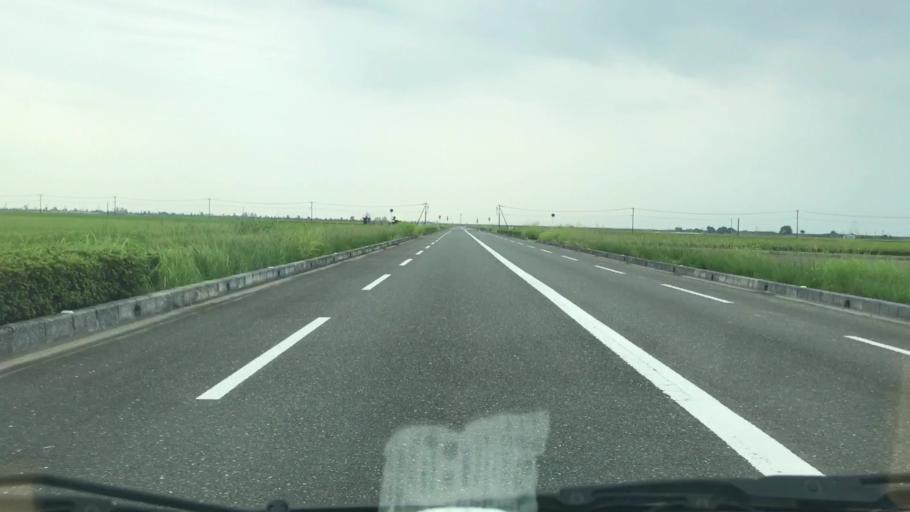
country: JP
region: Saga Prefecture
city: Okawa
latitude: 33.1748
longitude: 130.2965
